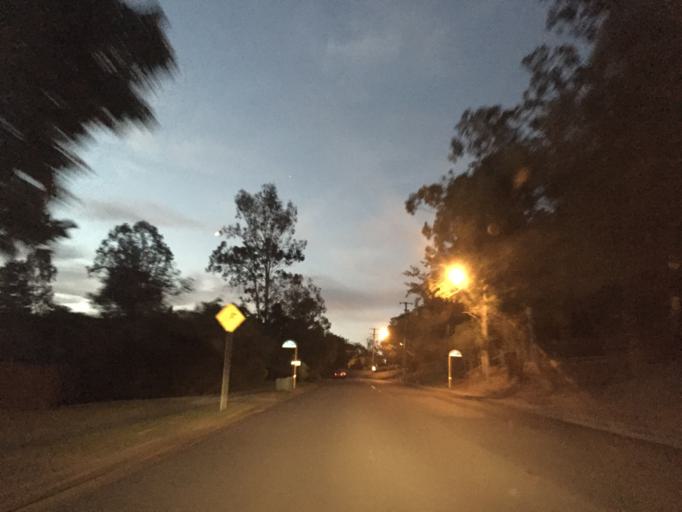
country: AU
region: Queensland
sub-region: Moreton Bay
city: Ferny Hills
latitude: -27.4438
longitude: 152.9399
